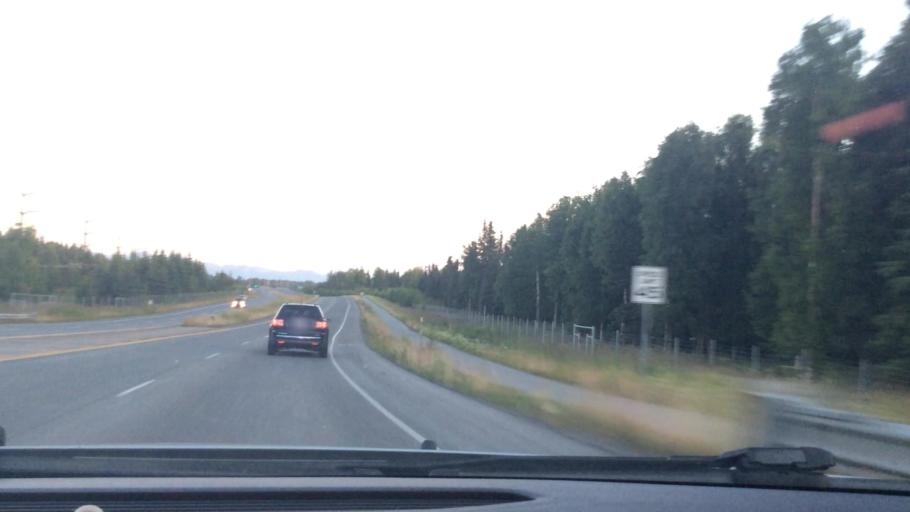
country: US
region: Alaska
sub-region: Anchorage Municipality
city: Anchorage
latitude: 61.1748
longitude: -149.8084
